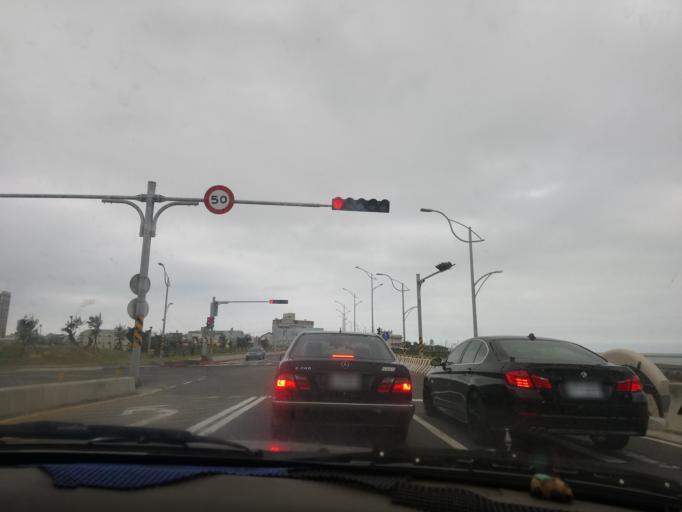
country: TW
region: Taiwan
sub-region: Hsinchu
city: Hsinchu
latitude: 24.8457
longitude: 120.9330
